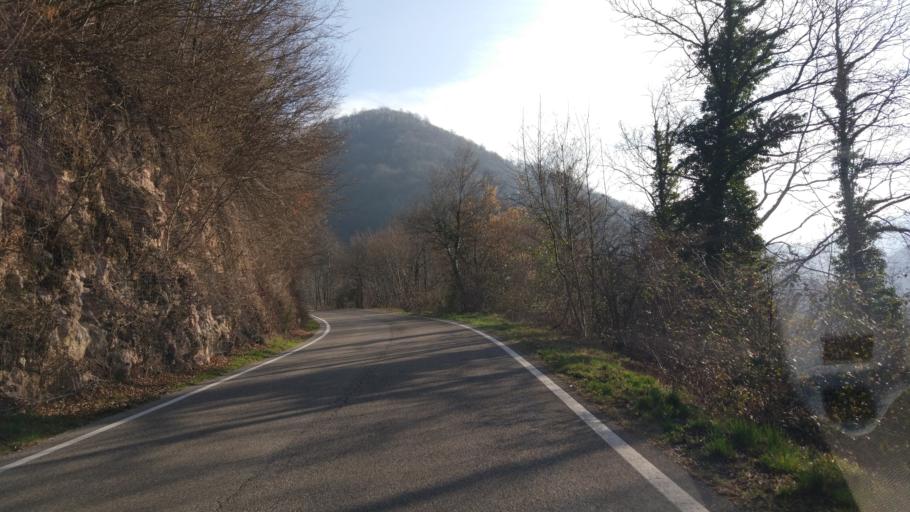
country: IT
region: Veneto
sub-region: Provincia di Verona
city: Selva di Progno
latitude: 45.6021
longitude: 11.1627
